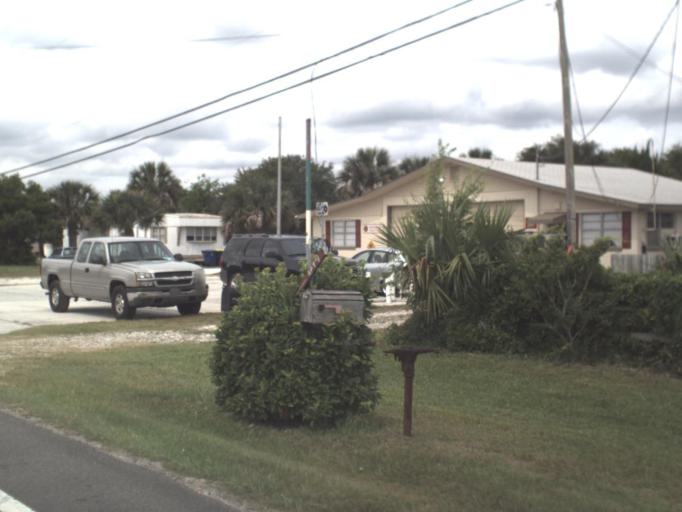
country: US
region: Florida
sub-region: Duval County
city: Atlantic Beach
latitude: 30.3919
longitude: -81.4397
